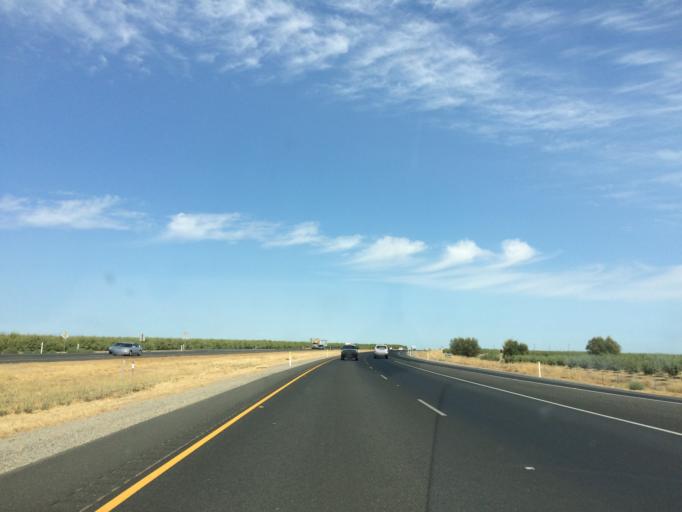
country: US
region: California
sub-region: Yolo County
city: Dunnigan
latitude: 38.9270
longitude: -122.0009
